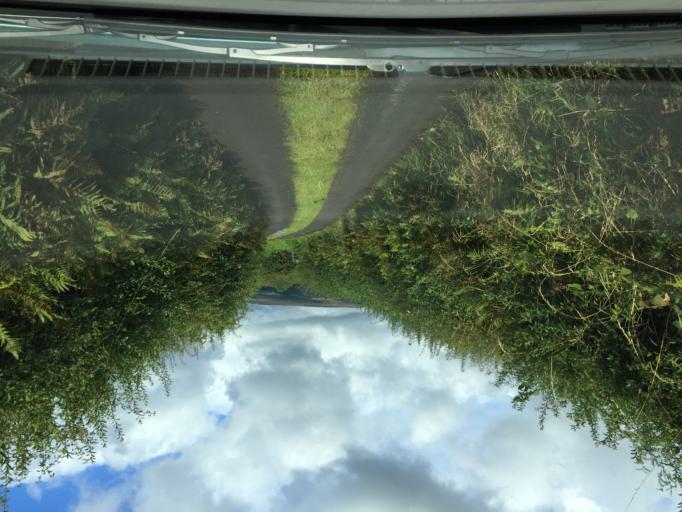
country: IE
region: Connaught
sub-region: Maigh Eo
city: Swinford
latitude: 54.0316
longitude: -8.8982
